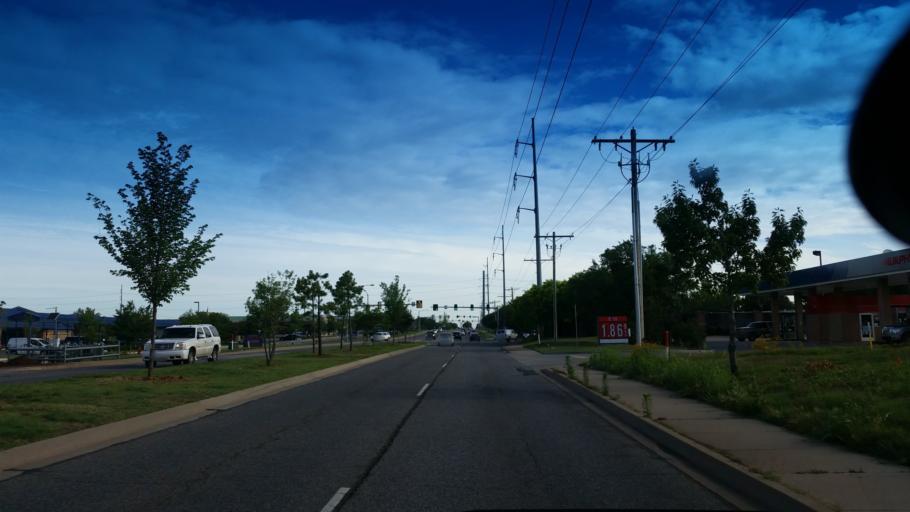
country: US
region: Oklahoma
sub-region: Oklahoma County
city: Edmond
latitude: 35.6642
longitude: -97.5140
